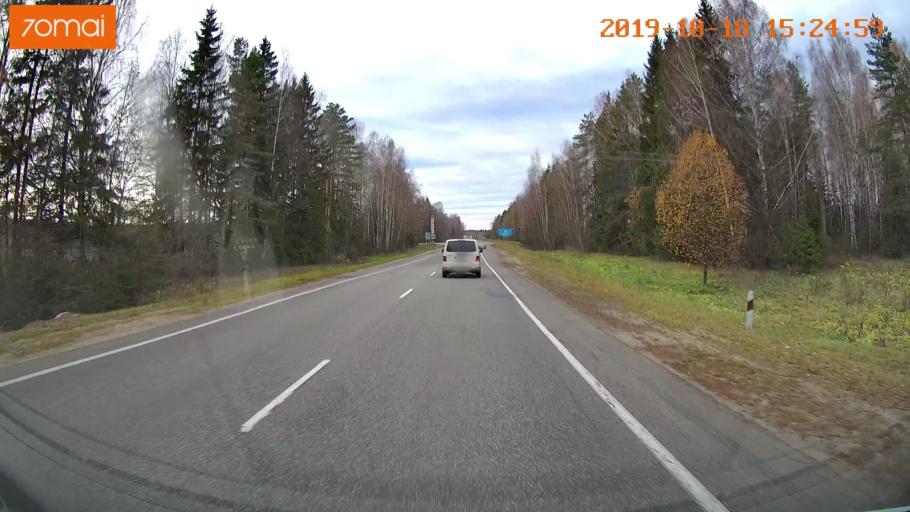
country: RU
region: Vladimir
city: Anopino
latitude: 55.7383
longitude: 40.7138
